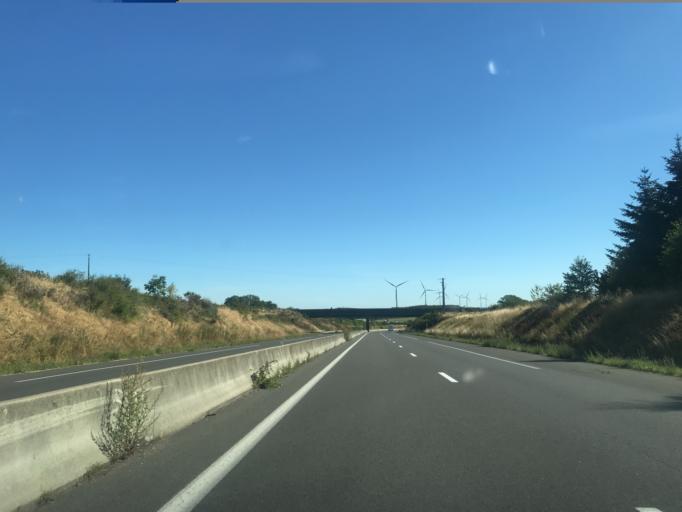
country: FR
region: Auvergne
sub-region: Departement de l'Allier
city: Huriel
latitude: 46.3001
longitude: 2.4374
